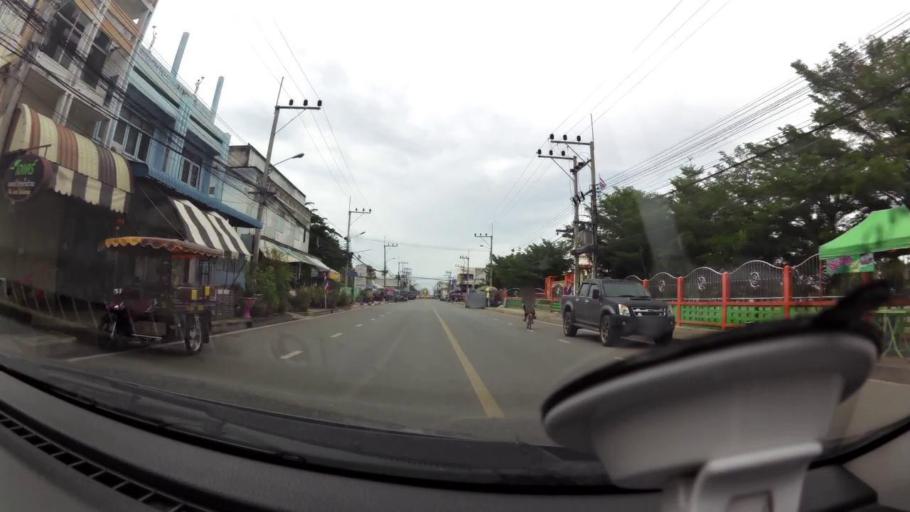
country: TH
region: Prachuap Khiri Khan
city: Pran Buri
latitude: 12.4006
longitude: 99.9910
